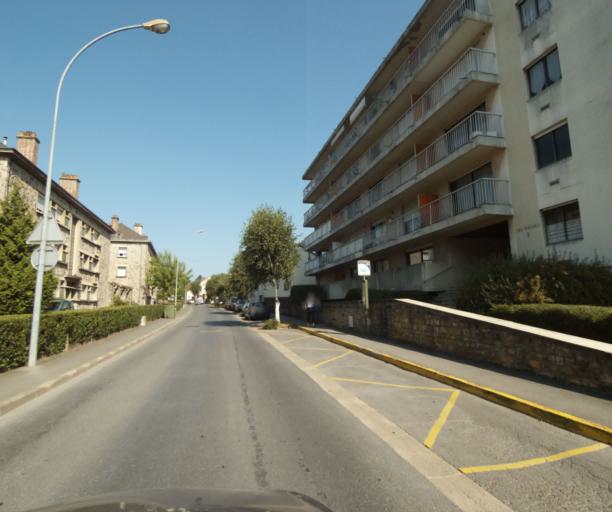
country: FR
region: Champagne-Ardenne
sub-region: Departement des Ardennes
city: Charleville-Mezieres
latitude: 49.7812
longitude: 4.7146
